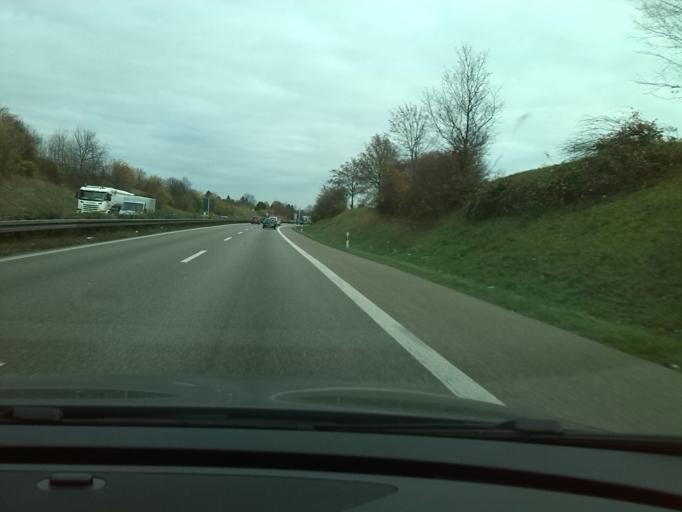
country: DE
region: Baden-Wuerttemberg
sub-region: Regierungsbezirk Stuttgart
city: Fellbach
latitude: 48.7950
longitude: 9.2531
